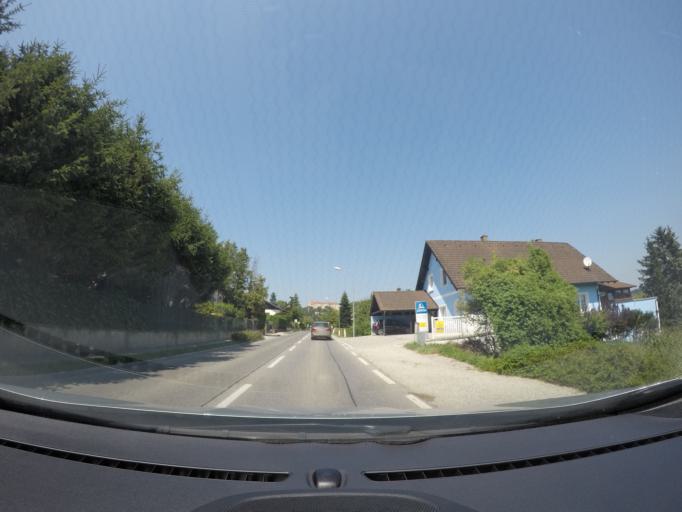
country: AT
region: Lower Austria
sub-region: Politischer Bezirk Sankt Polten
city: Maria-Anzbach
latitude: 48.1934
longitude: 15.9173
